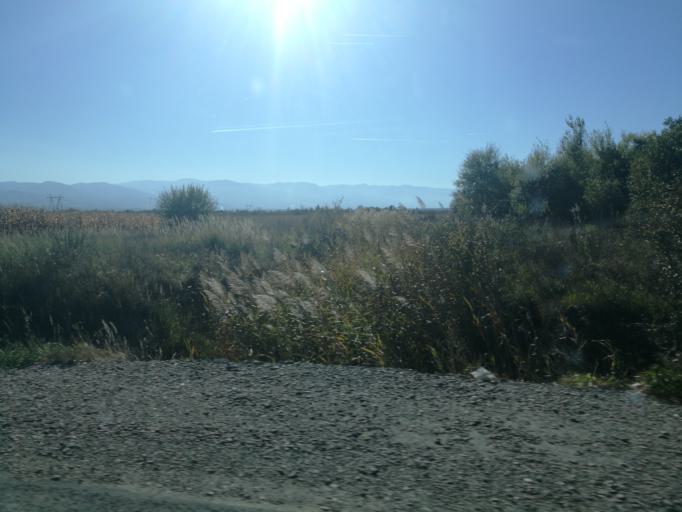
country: RO
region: Brasov
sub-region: Comuna Sinca Veche
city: Sinca Veche
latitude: 45.8011
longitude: 25.1776
